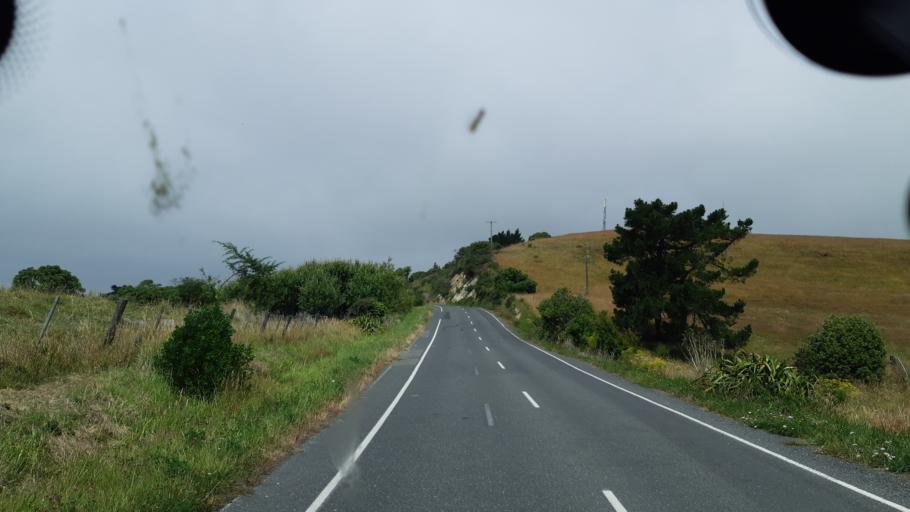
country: NZ
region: Canterbury
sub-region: Kaikoura District
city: Kaikoura
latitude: -42.4172
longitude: 173.6895
